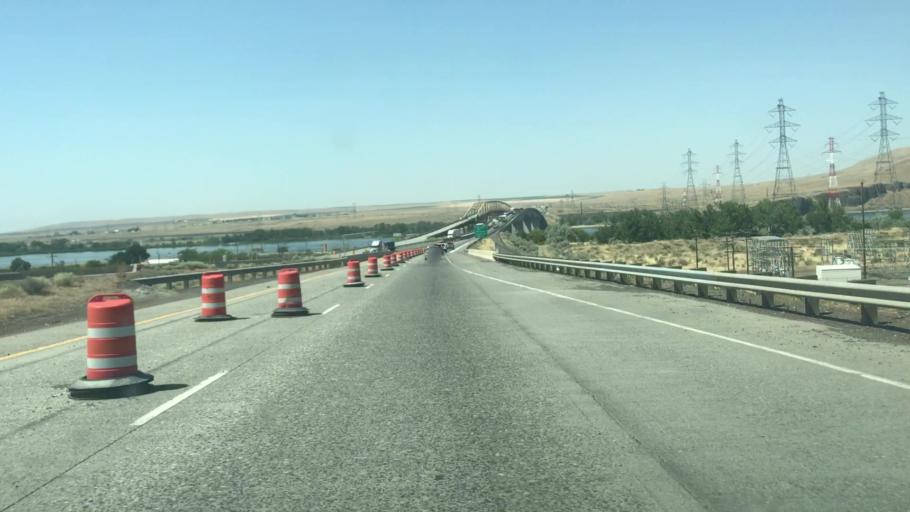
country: US
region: Oregon
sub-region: Umatilla County
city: Umatilla
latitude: 45.9226
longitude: -119.3234
